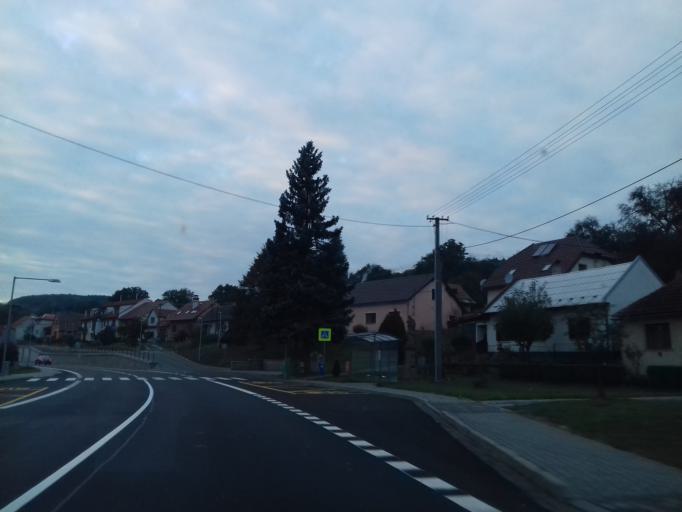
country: CZ
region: Zlin
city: Bojkovice
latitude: 48.9638
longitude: 17.8700
